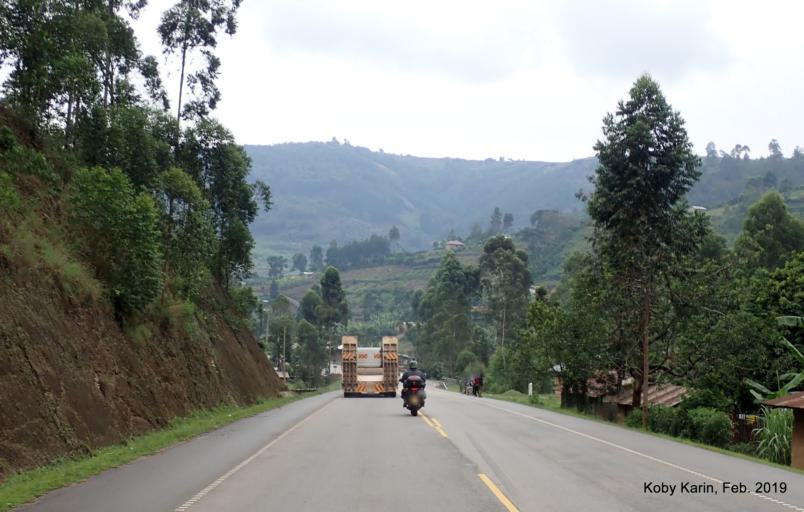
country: UG
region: Western Region
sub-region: Kabale District
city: Kabale
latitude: -1.1773
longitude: 30.1121
